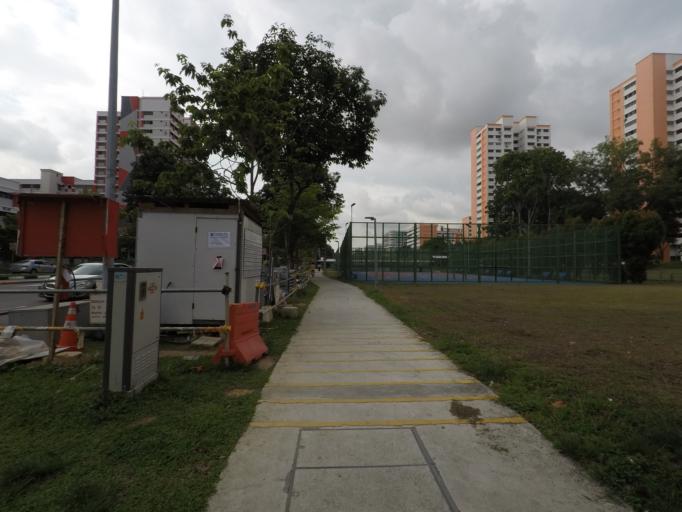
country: MY
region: Johor
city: Kampung Pasir Gudang Baru
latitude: 1.3796
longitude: 103.8927
